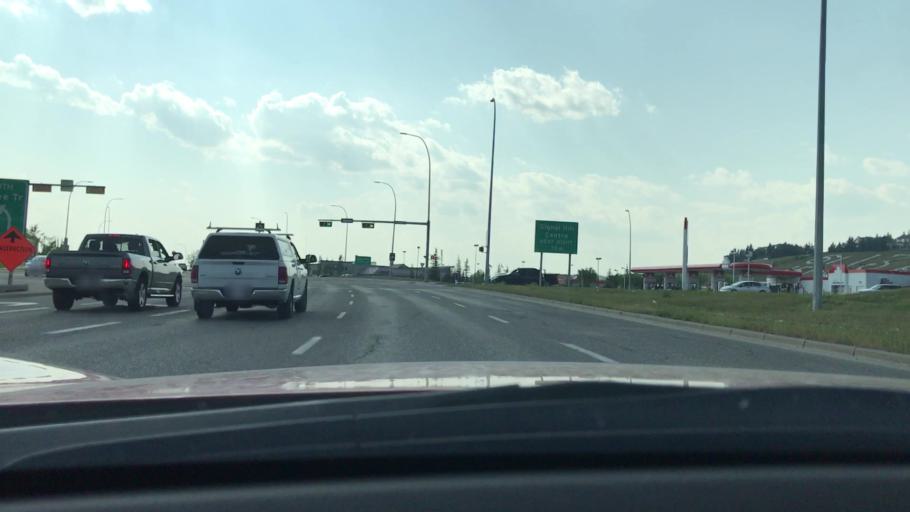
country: CA
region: Alberta
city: Calgary
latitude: 51.0182
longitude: -114.1650
